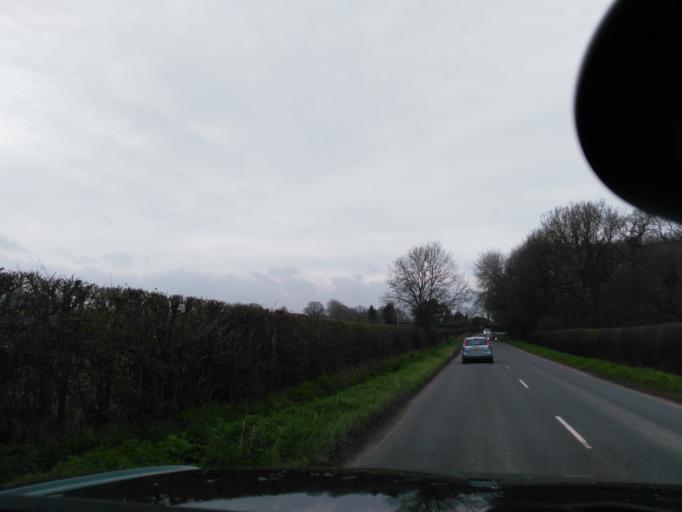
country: GB
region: England
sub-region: Wiltshire
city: Wingfield
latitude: 51.3045
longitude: -2.2579
